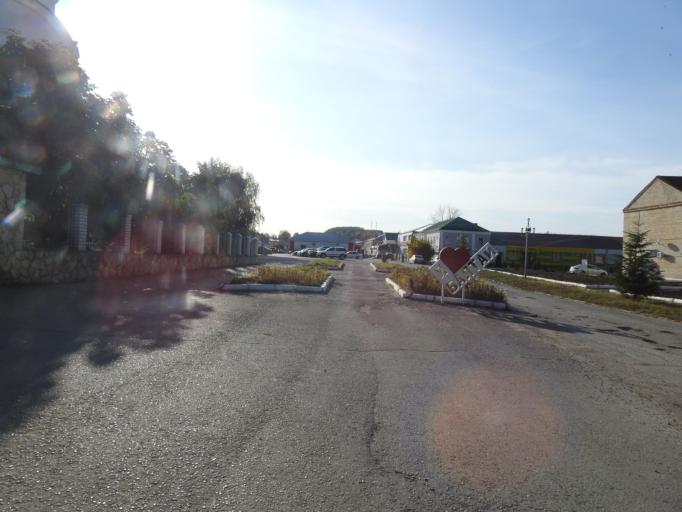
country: RU
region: Saratov
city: Baltay
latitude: 52.4675
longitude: 46.6279
